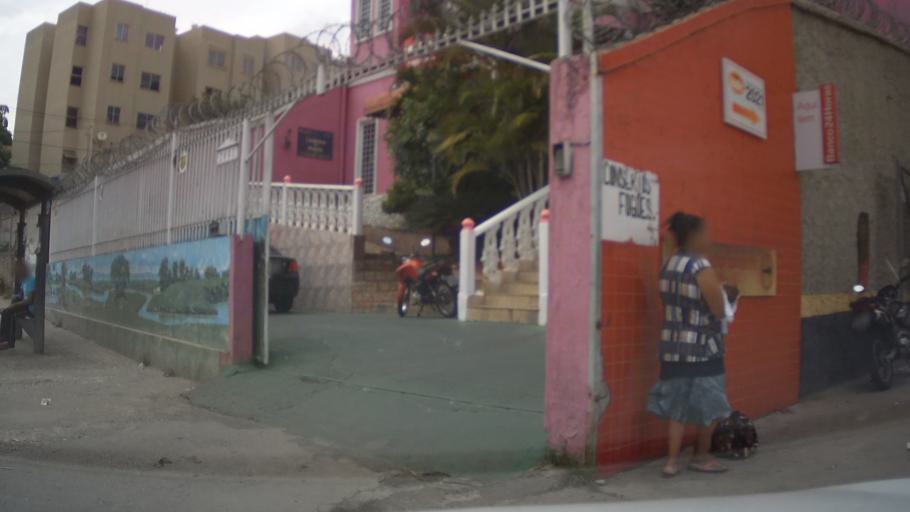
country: BR
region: Minas Gerais
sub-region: Belo Horizonte
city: Belo Horizonte
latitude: -19.8111
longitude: -43.9671
